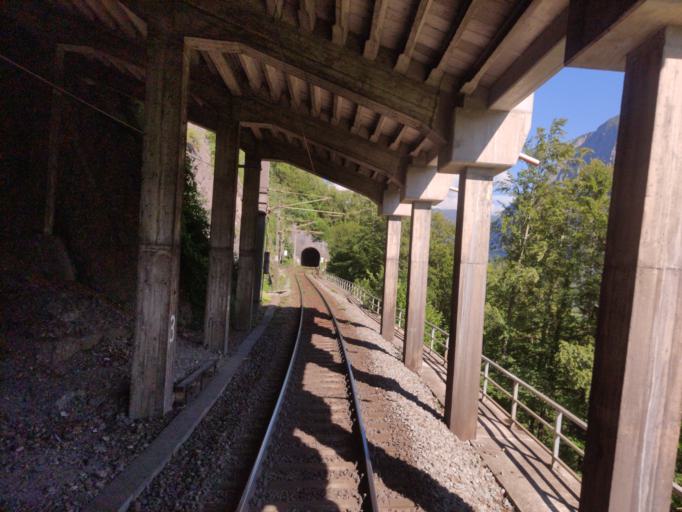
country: AT
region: Vorarlberg
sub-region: Politischer Bezirk Bludenz
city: Innerbraz
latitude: 47.1459
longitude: 9.9257
